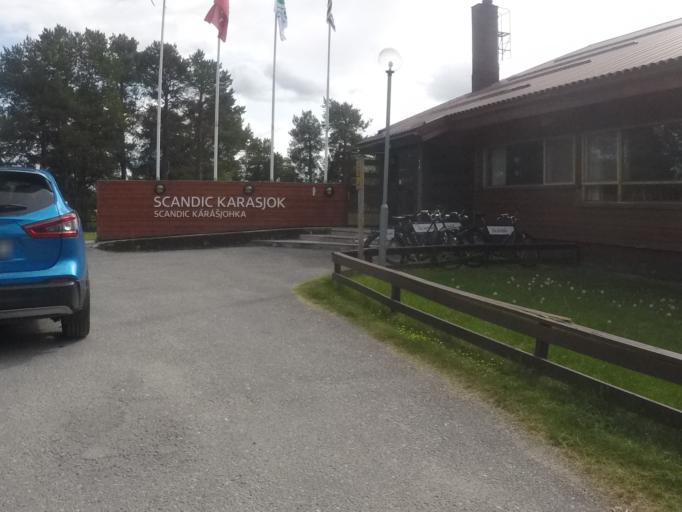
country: NO
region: Finnmark Fylke
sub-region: Karasjok
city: Karasjohka
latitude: 69.4737
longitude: 25.5100
